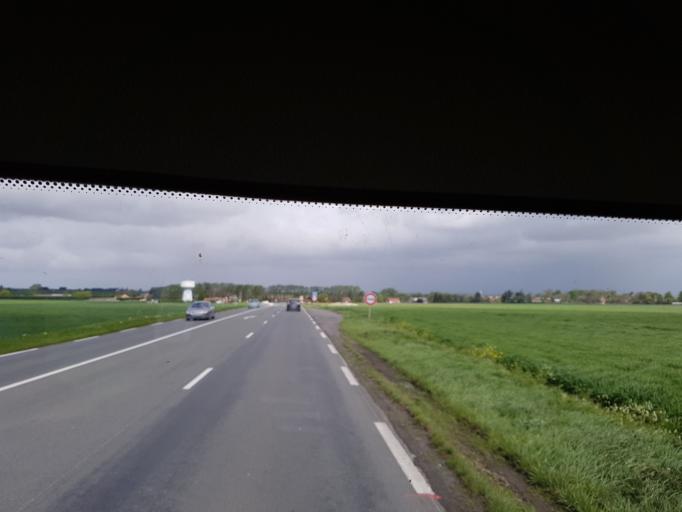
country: FR
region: Nord-Pas-de-Calais
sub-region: Departement du Nord
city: Raillencourt-Sainte-Olle
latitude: 50.2057
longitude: 3.1941
